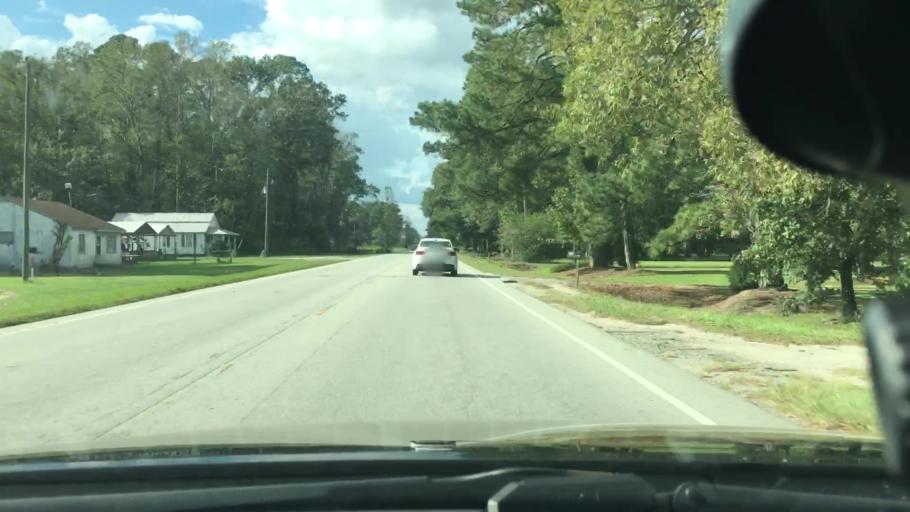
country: US
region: North Carolina
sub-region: Craven County
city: Vanceboro
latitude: 35.2648
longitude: -77.1054
